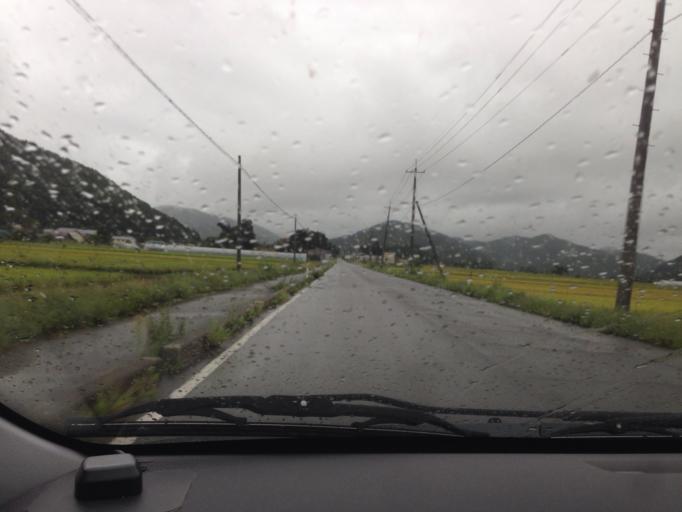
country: JP
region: Fukushima
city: Inawashiro
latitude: 37.4064
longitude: 140.1278
